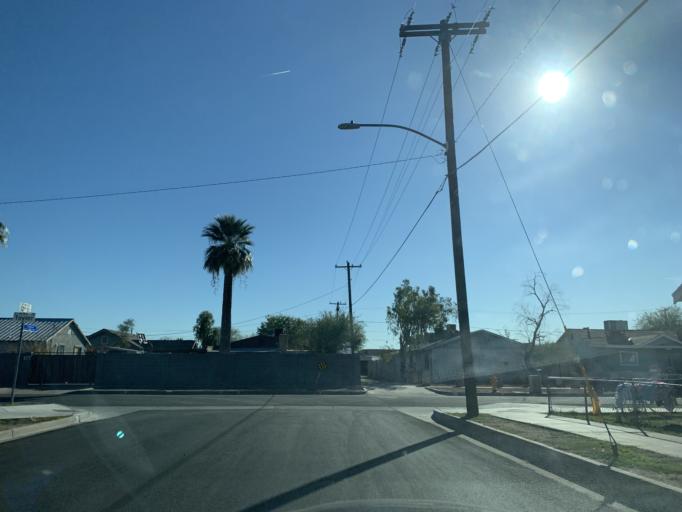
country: US
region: Arizona
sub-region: Maricopa County
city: Phoenix
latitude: 33.4541
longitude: -112.0565
